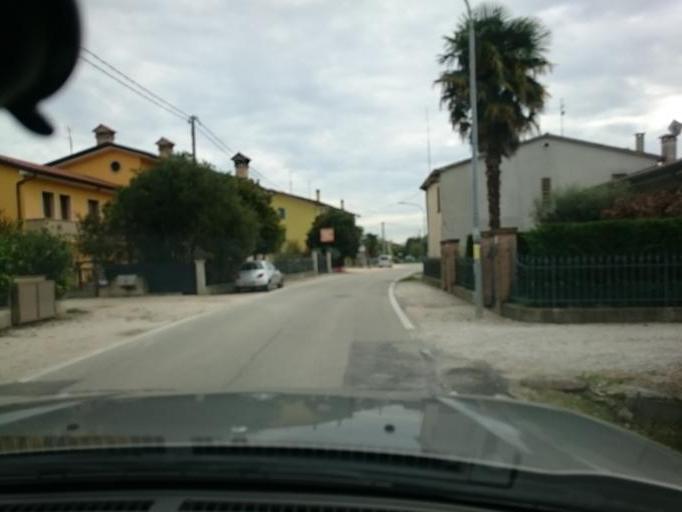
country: IT
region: Veneto
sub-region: Provincia di Padova
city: Arzergrande
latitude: 45.2846
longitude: 12.0602
